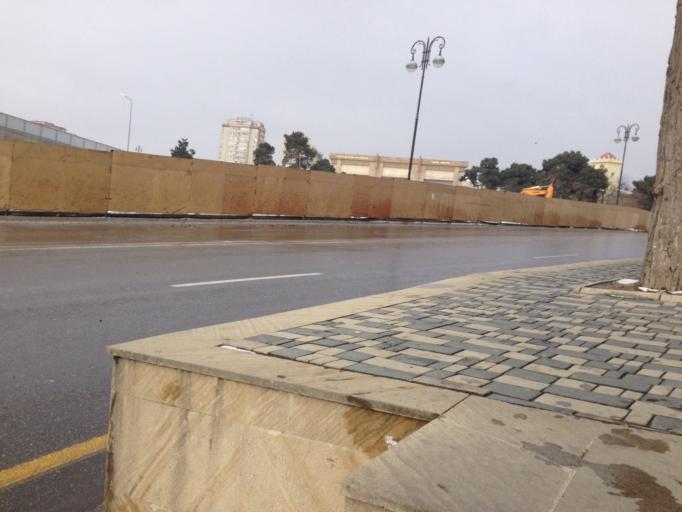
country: AZ
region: Baki
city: Baku
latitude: 40.3975
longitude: 49.8505
